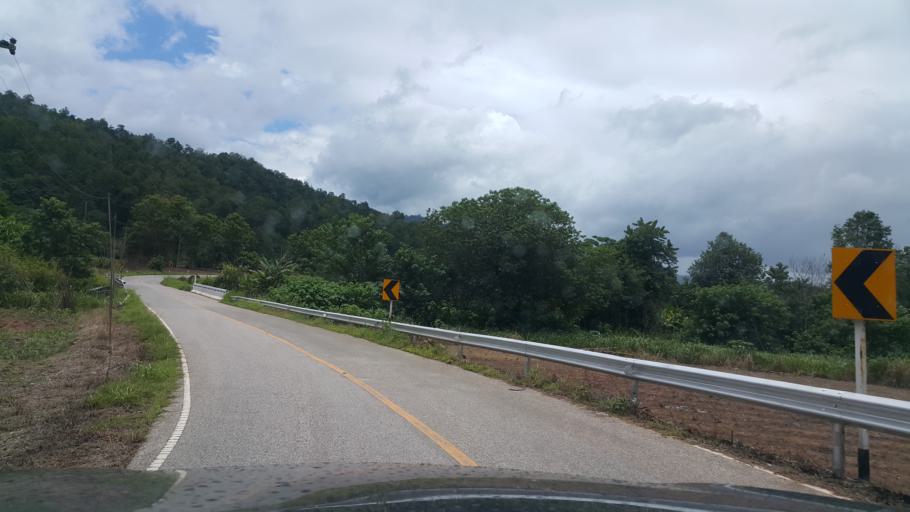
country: TH
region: Loei
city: Na Haeo
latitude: 17.5507
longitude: 100.8427
